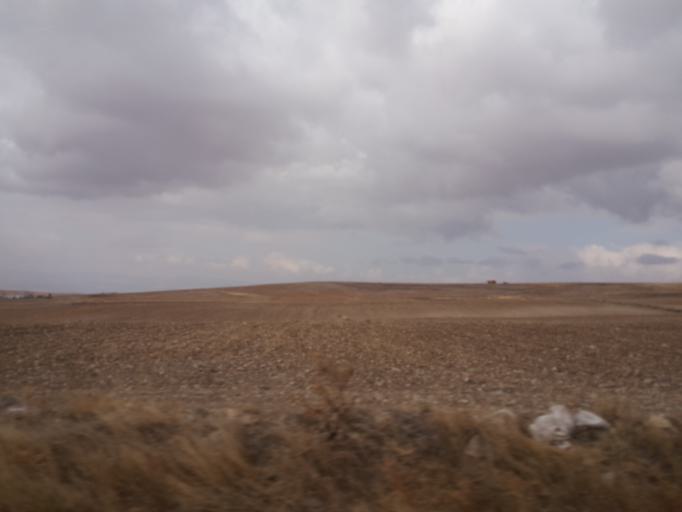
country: TR
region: Kirikkale
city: Keskin
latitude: 39.6448
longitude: 33.6189
